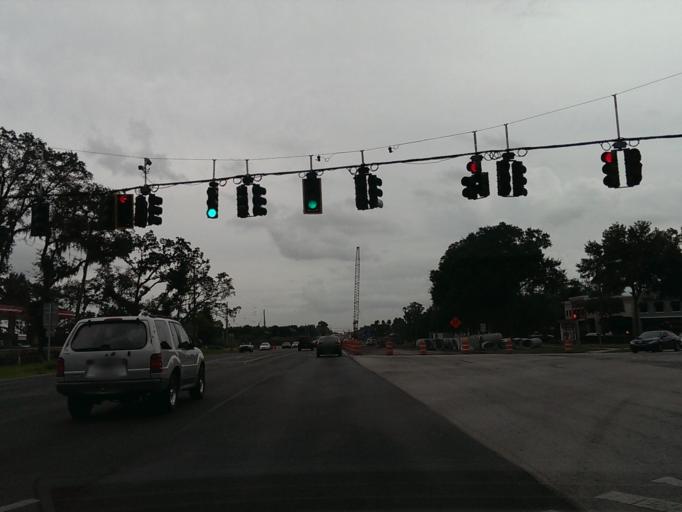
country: US
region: Florida
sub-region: Orange County
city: Ocoee
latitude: 28.5517
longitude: -81.5383
